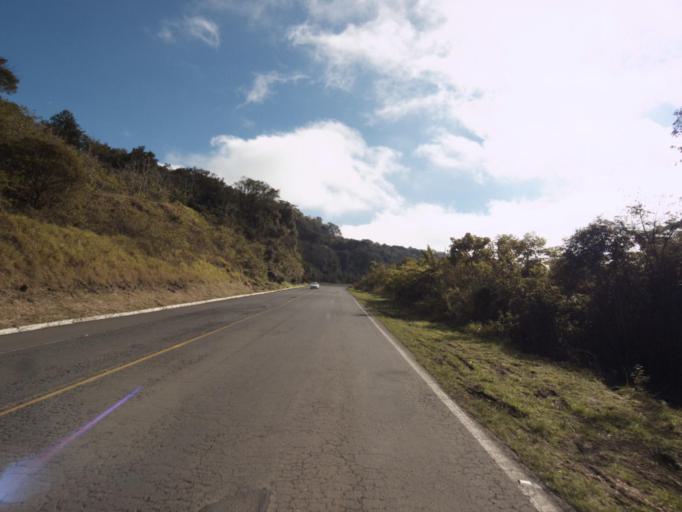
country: BR
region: Rio Grande do Sul
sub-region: Frederico Westphalen
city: Frederico Westphalen
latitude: -27.1343
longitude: -53.2127
